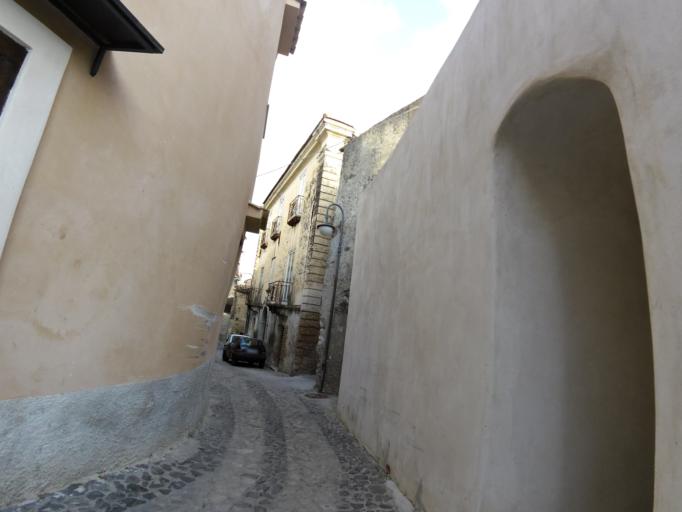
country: IT
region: Calabria
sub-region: Provincia di Reggio Calabria
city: Caulonia
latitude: 38.3803
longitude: 16.4082
